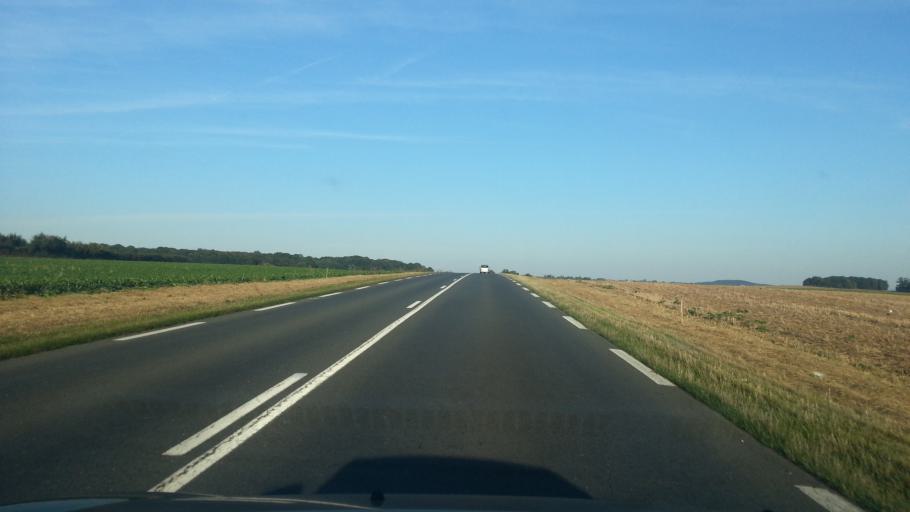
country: FR
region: Picardie
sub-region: Departement de l'Oise
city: Catenoy
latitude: 49.3759
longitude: 2.5328
